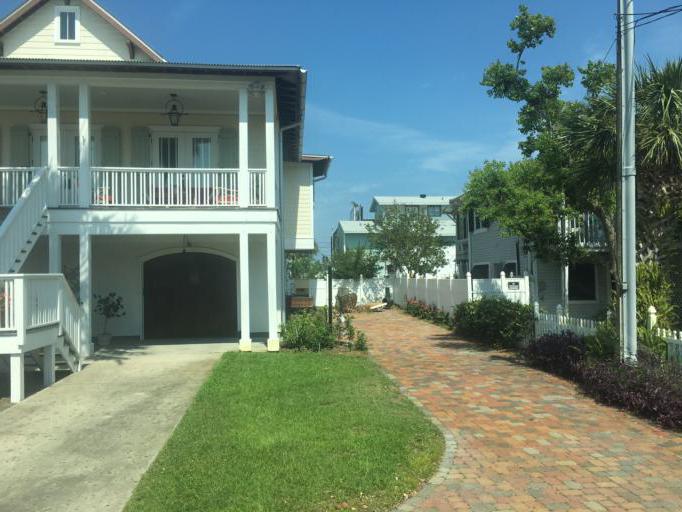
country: US
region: Florida
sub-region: Bay County
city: Lower Grand Lagoon
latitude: 30.1433
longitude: -85.7511
